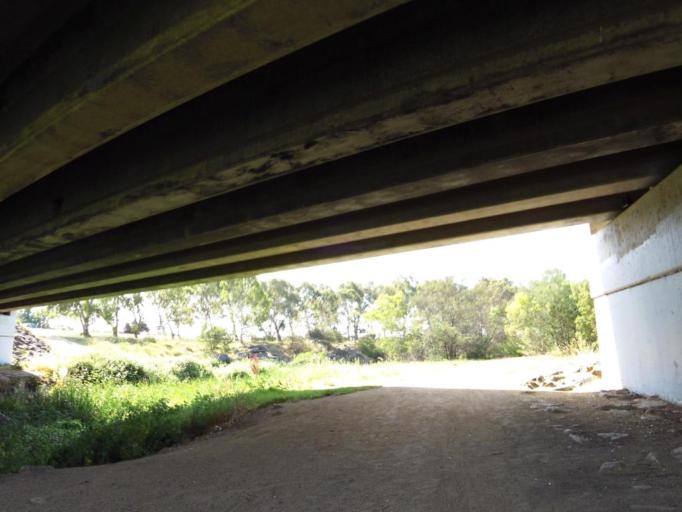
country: AU
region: Victoria
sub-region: Whittlesea
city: Epping
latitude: -37.6451
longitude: 145.0317
